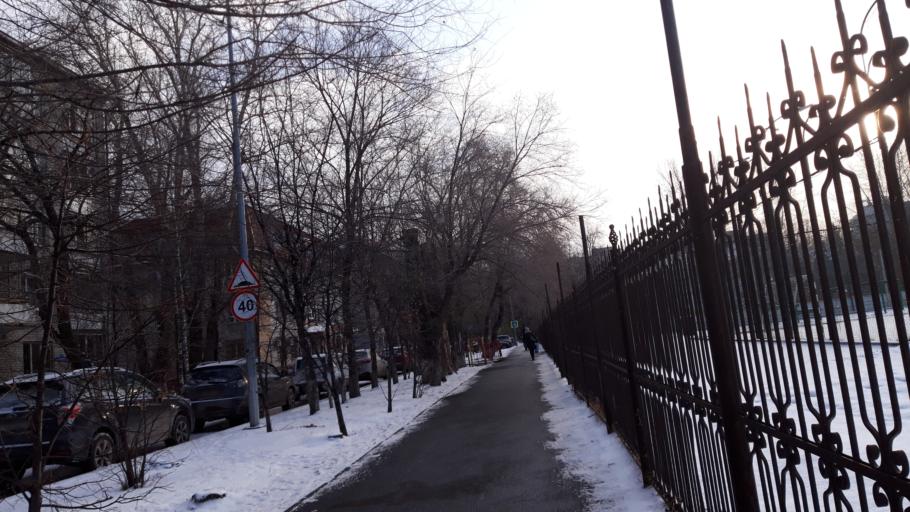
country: RU
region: Tjumen
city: Tyumen
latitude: 57.1522
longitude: 65.5484
